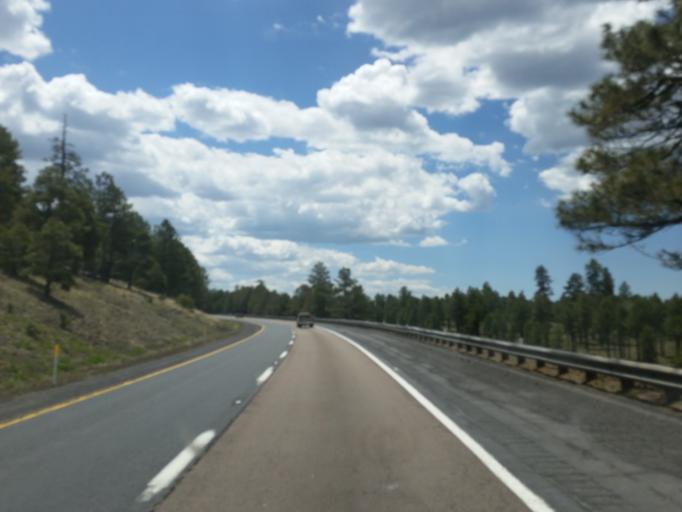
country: US
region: Arizona
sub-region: Coconino County
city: Flagstaff
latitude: 35.2073
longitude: -111.7711
